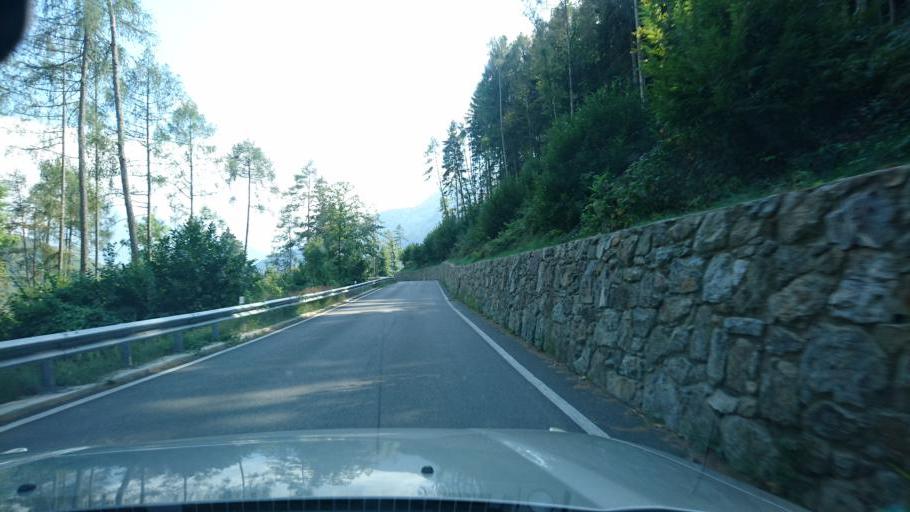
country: IT
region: Lombardy
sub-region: Provincia di Brescia
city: Berzo
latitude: 46.0975
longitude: 10.3091
